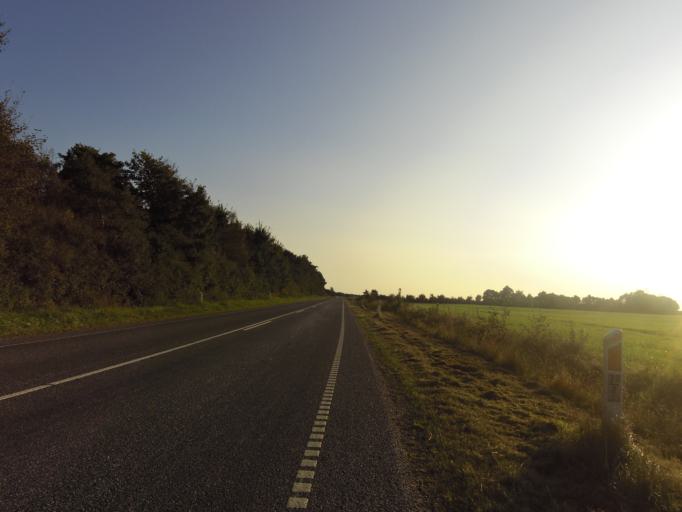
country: DK
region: South Denmark
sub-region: Vejen Kommune
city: Vejen
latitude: 55.4191
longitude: 9.1394
